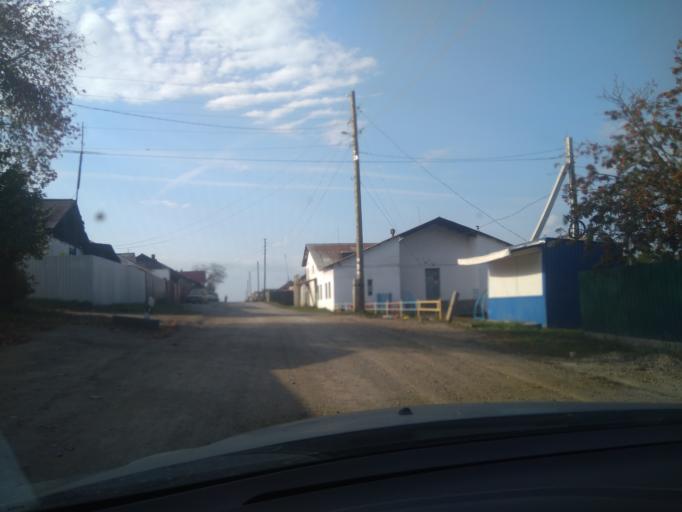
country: RU
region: Sverdlovsk
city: Pokrovskoye
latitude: 56.4337
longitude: 61.5924
